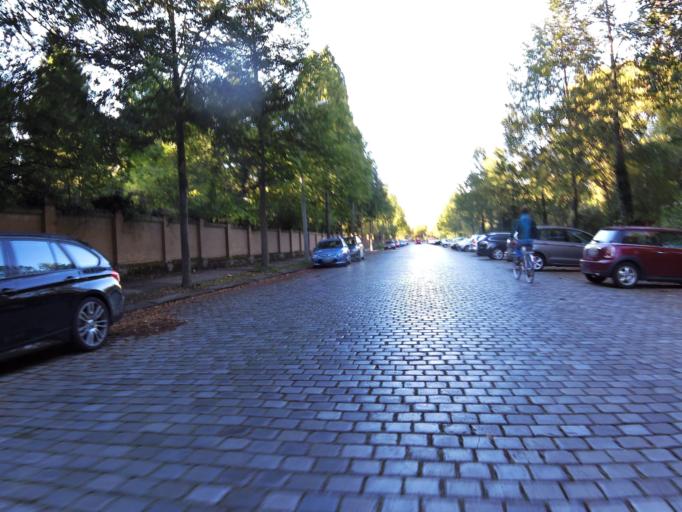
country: DE
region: Saxony
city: Leipzig
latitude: 51.3286
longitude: 12.3928
